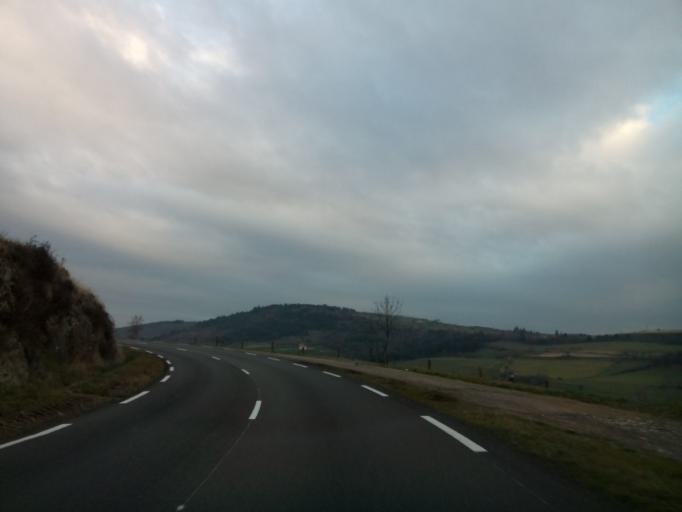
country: FR
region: Rhone-Alpes
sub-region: Departement de la Loire
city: Saint-Julien-Molin-Molette
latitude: 45.3251
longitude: 4.6297
